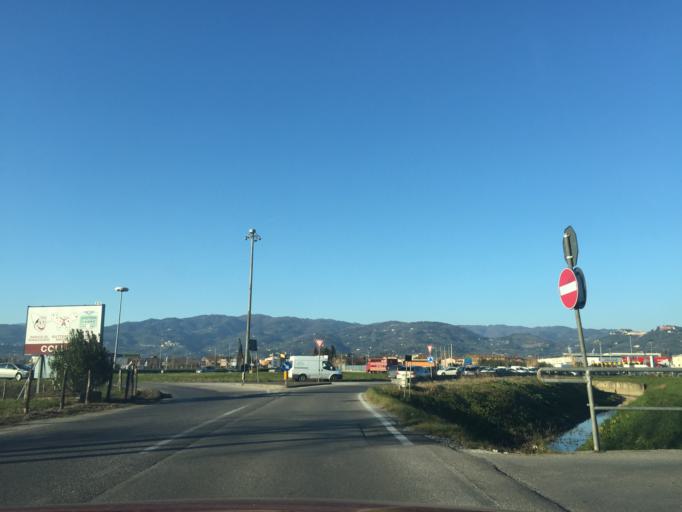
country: IT
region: Tuscany
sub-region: Provincia di Pistoia
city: Margine Coperta-Traversagna
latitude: 43.8605
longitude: 10.7671
